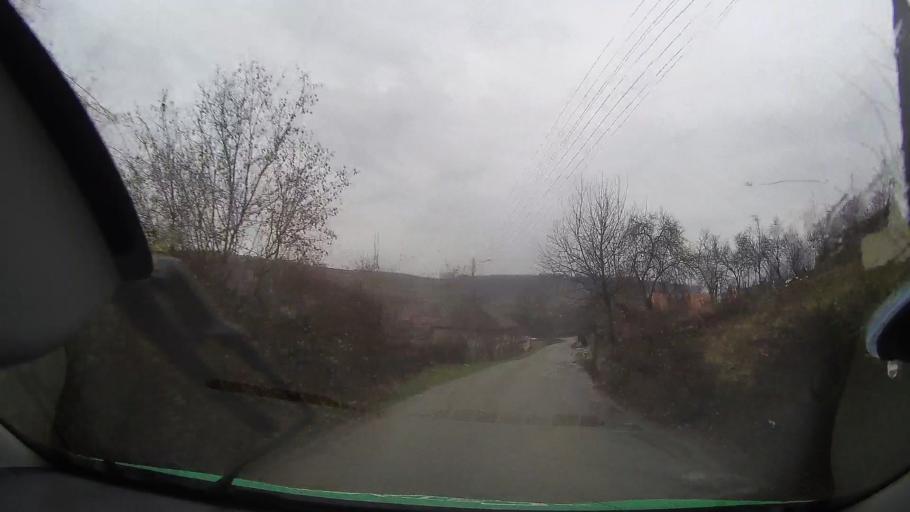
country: RO
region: Bihor
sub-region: Comuna Uileacu de Beius
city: Forau
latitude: 46.7137
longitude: 22.2284
